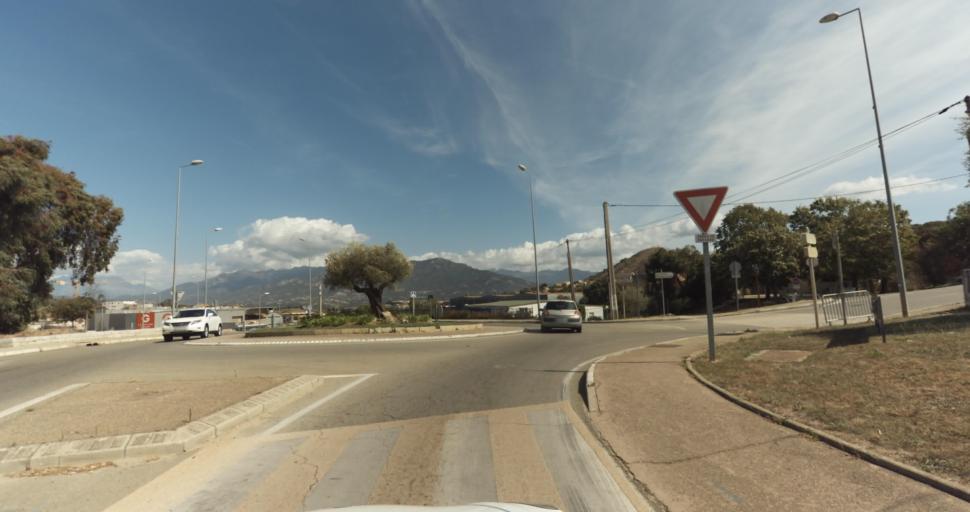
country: FR
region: Corsica
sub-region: Departement de la Corse-du-Sud
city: Alata
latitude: 41.9500
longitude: 8.7711
